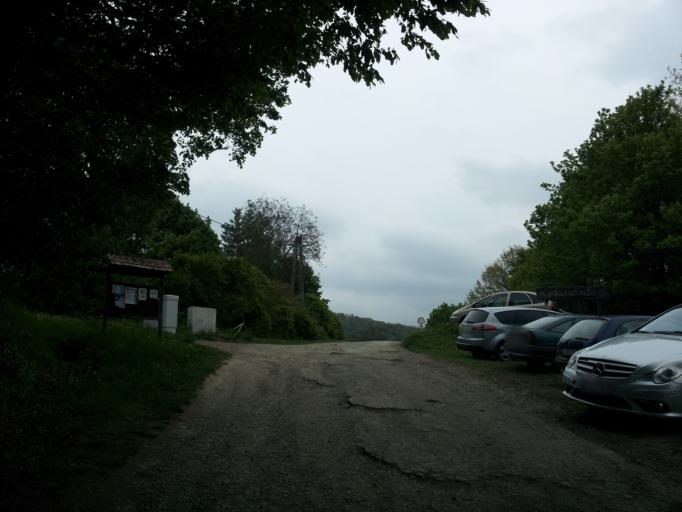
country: HU
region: Baranya
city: Hosszuheteny
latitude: 46.1870
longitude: 18.3577
